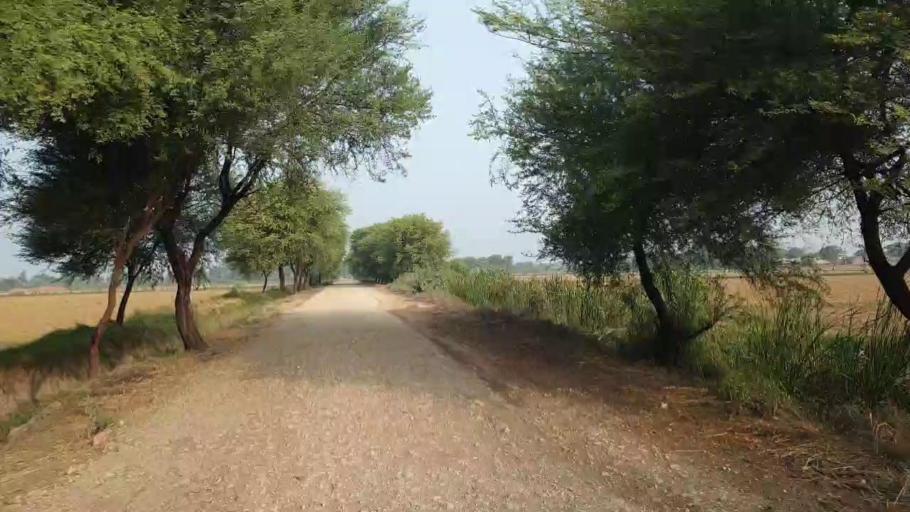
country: PK
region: Sindh
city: Tando Muhammad Khan
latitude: 25.1358
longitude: 68.5938
